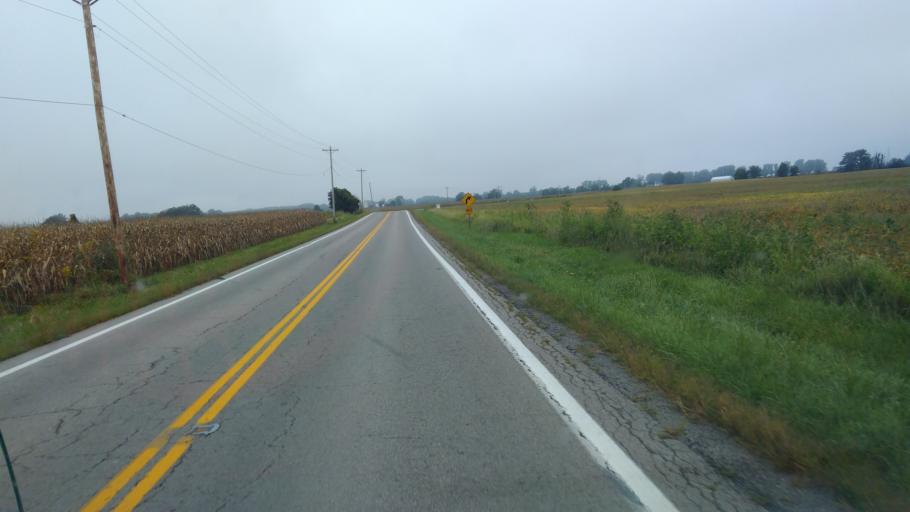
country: US
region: Ohio
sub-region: Logan County
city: Northwood
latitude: 40.4721
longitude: -83.5780
